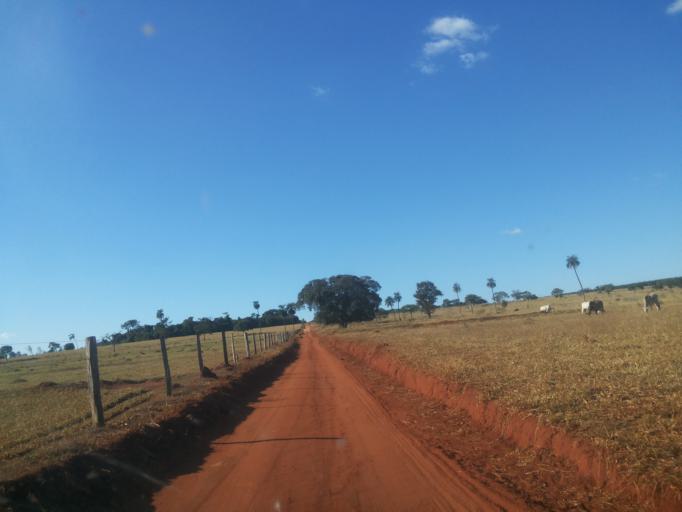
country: BR
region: Minas Gerais
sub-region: Centralina
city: Centralina
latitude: -18.7305
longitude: -49.1603
